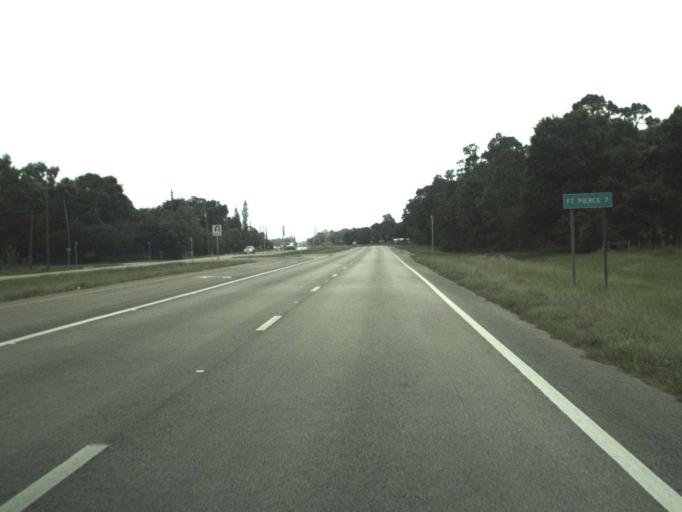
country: US
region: Florida
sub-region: Saint Lucie County
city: Fort Pierce South
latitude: 27.4021
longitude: -80.4452
